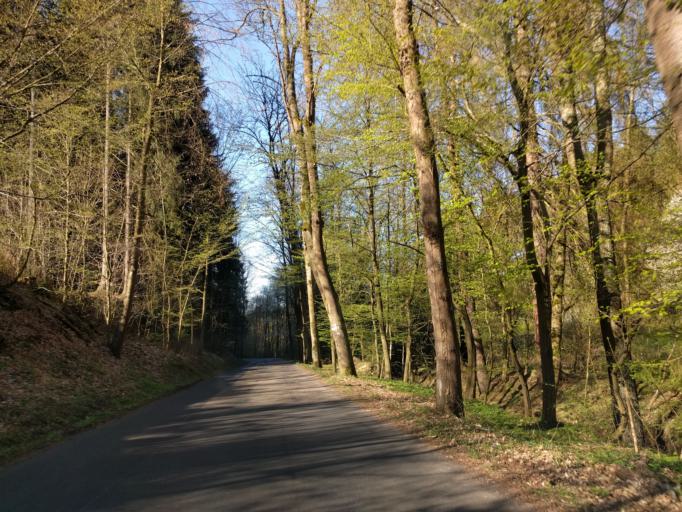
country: CZ
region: Central Bohemia
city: Ondrejov
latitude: 49.8982
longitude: 14.7395
